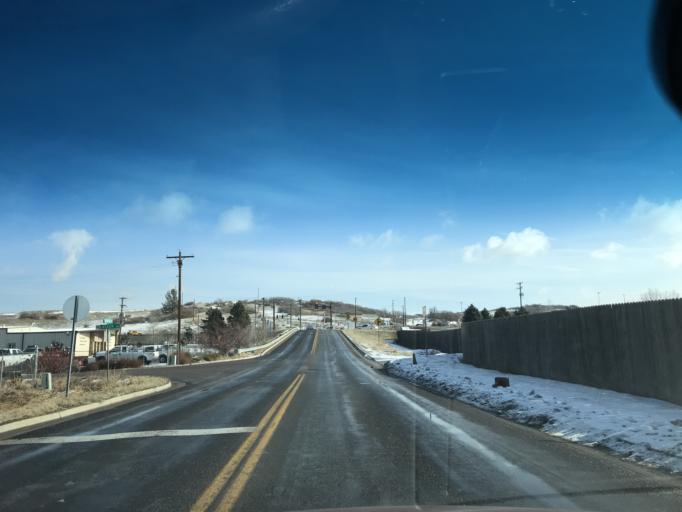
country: US
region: Colorado
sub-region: Douglas County
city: Highlands Ranch
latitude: 39.4710
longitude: -104.9911
